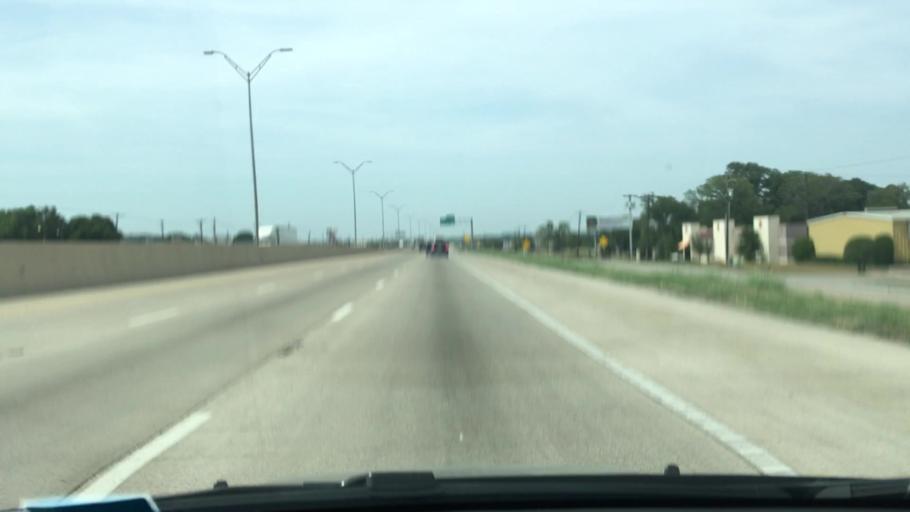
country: US
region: Texas
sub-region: Dallas County
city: Glenn Heights
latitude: 32.5692
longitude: -96.8224
